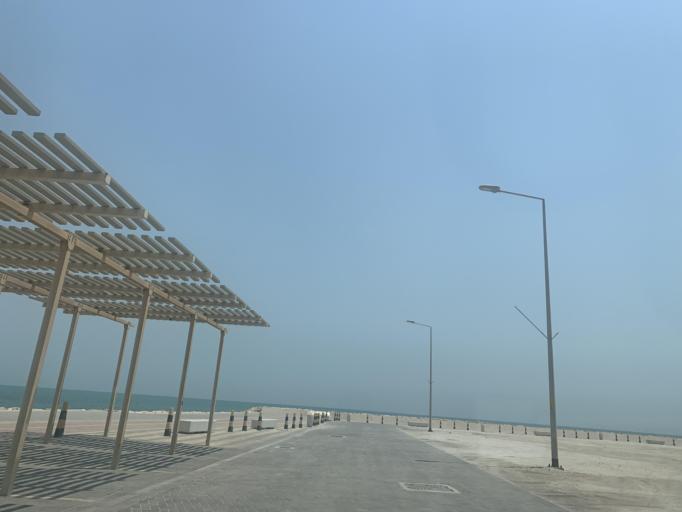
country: BH
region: Muharraq
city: Al Hadd
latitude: 26.2370
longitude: 50.6768
